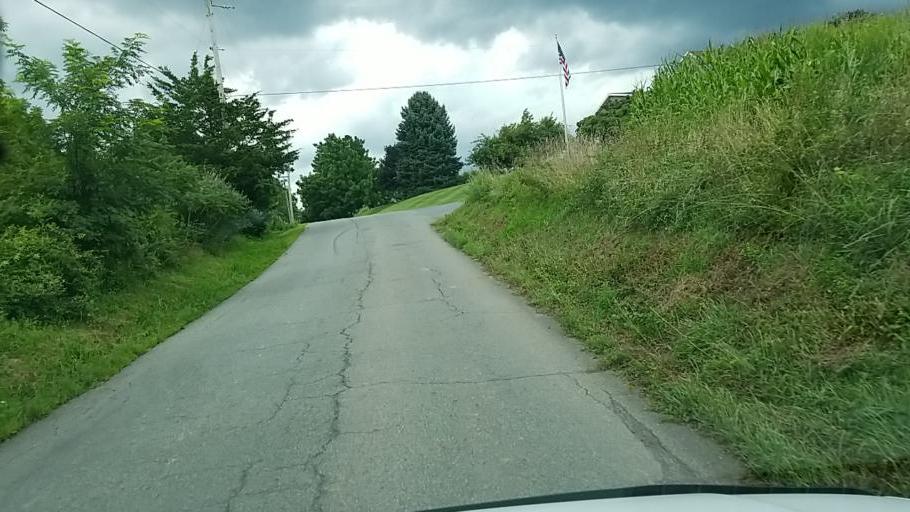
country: US
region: Pennsylvania
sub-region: Dauphin County
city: Elizabethville
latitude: 40.5934
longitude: -76.8021
